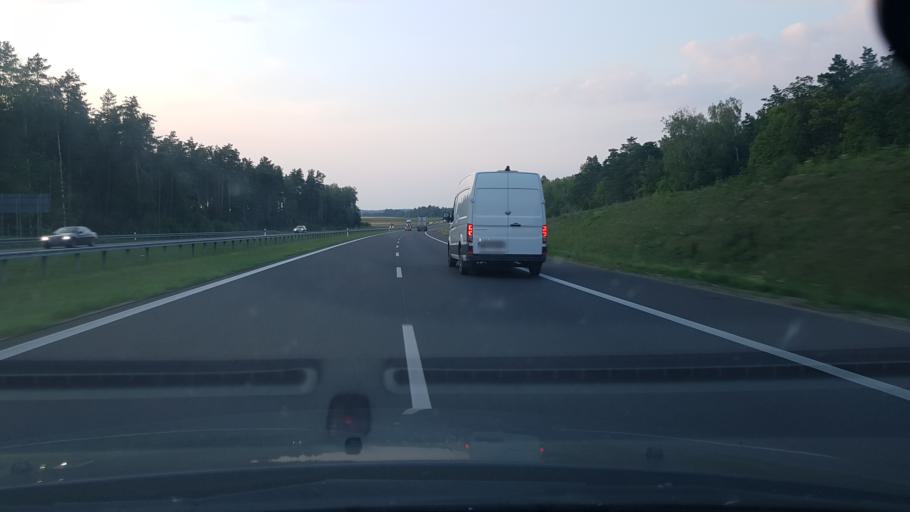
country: PL
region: Masovian Voivodeship
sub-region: Powiat mlawski
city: Wieczfnia Koscielna
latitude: 53.2538
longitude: 20.4244
